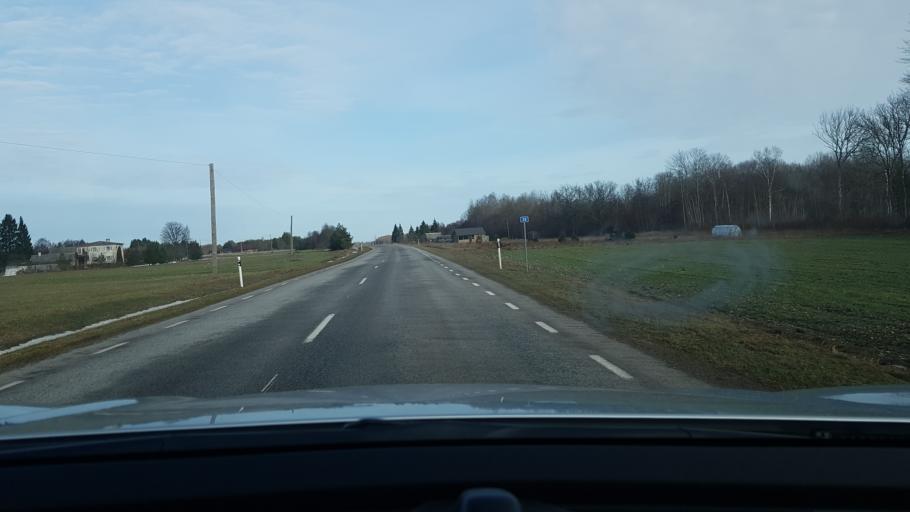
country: EE
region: Saare
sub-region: Kuressaare linn
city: Kuressaare
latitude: 58.5033
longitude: 22.7055
